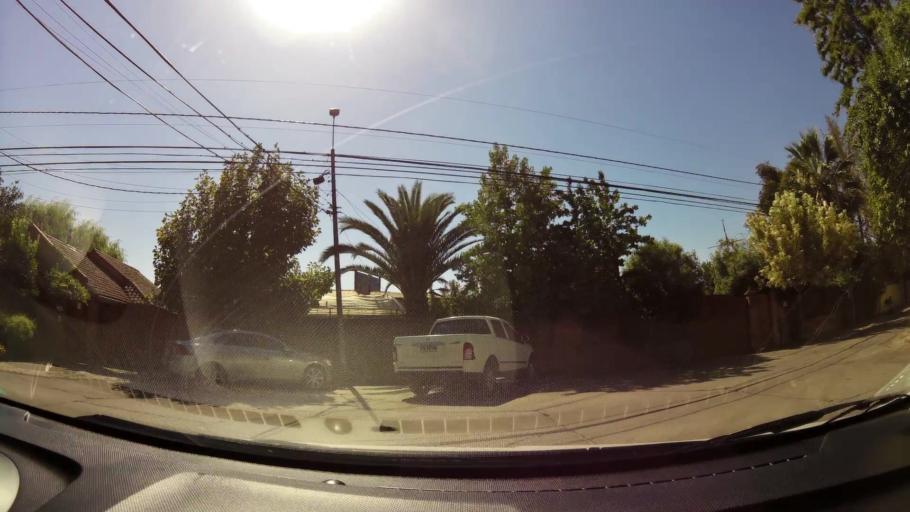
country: CL
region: Maule
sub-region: Provincia de Talca
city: Talca
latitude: -35.4316
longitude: -71.6209
